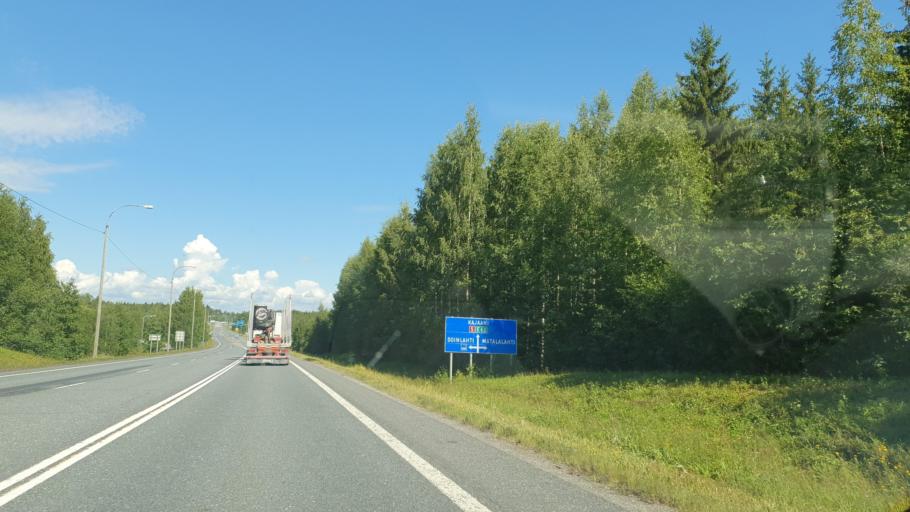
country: FI
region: Northern Savo
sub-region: Ylae-Savo
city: Iisalmi
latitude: 63.6226
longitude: 27.2247
